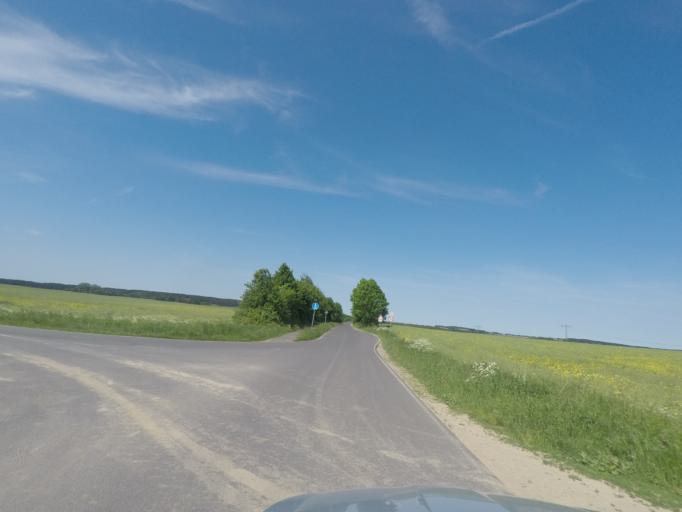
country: DE
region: Brandenburg
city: Britz
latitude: 52.8777
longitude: 13.7651
